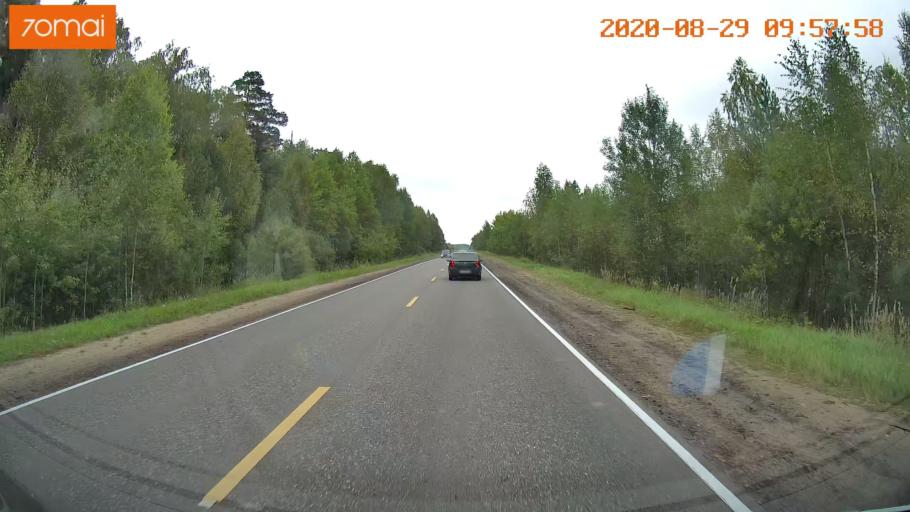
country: RU
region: Ivanovo
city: Zarechnyy
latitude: 57.4150
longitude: 42.3278
